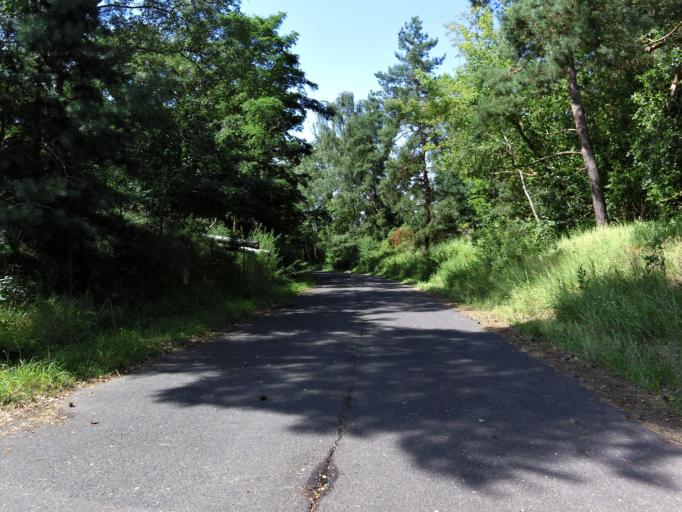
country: DE
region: Brandenburg
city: Furstenberg
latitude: 53.1925
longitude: 13.1706
